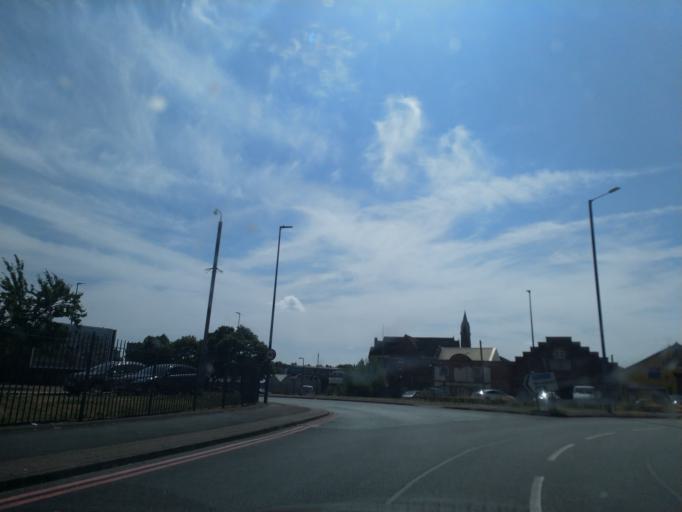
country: GB
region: England
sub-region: Sandwell
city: West Bromwich
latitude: 52.5084
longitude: -1.9904
